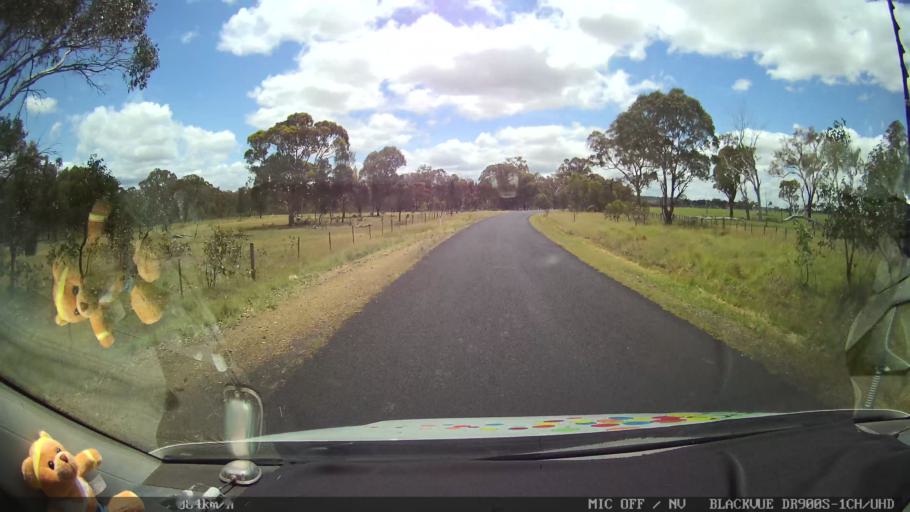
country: AU
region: New South Wales
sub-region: Glen Innes Severn
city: Glen Innes
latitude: -29.4204
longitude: 151.7156
